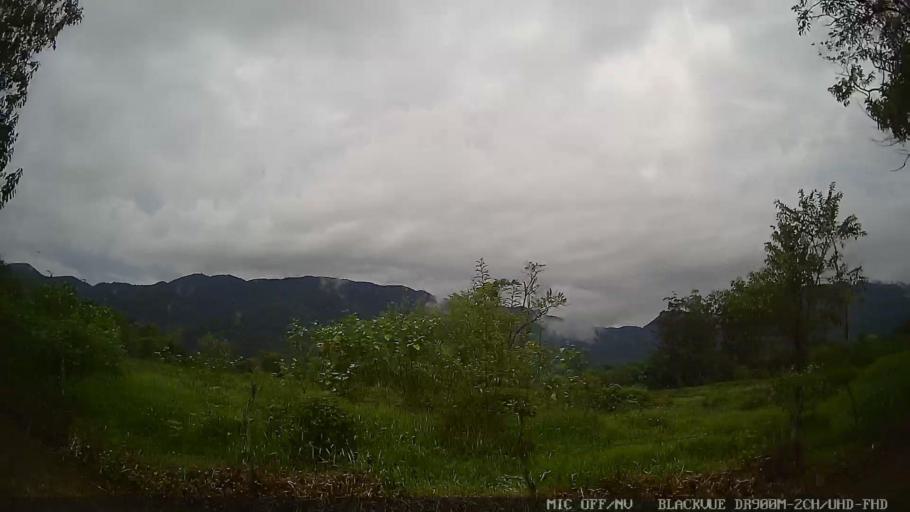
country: BR
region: Sao Paulo
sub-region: Sao Sebastiao
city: Sao Sebastiao
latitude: -23.7197
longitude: -45.4483
